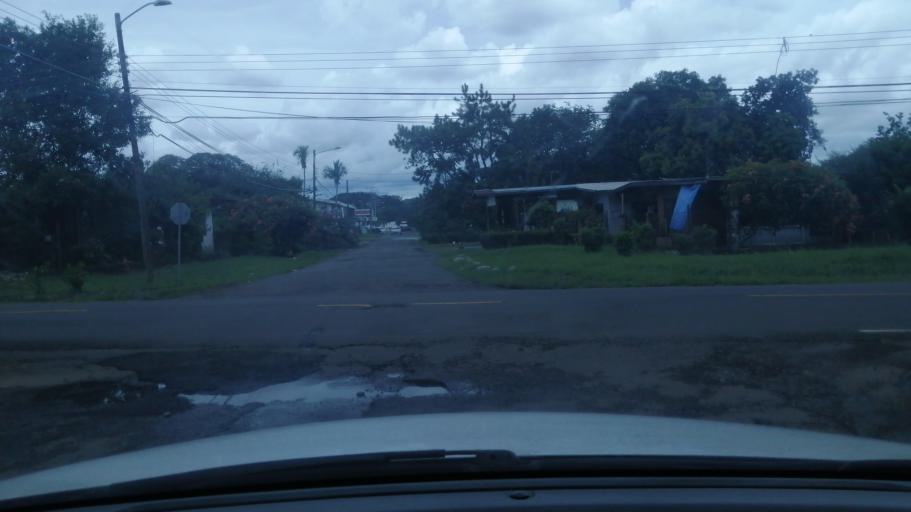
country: PA
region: Chiriqui
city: David
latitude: 8.4406
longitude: -82.4263
